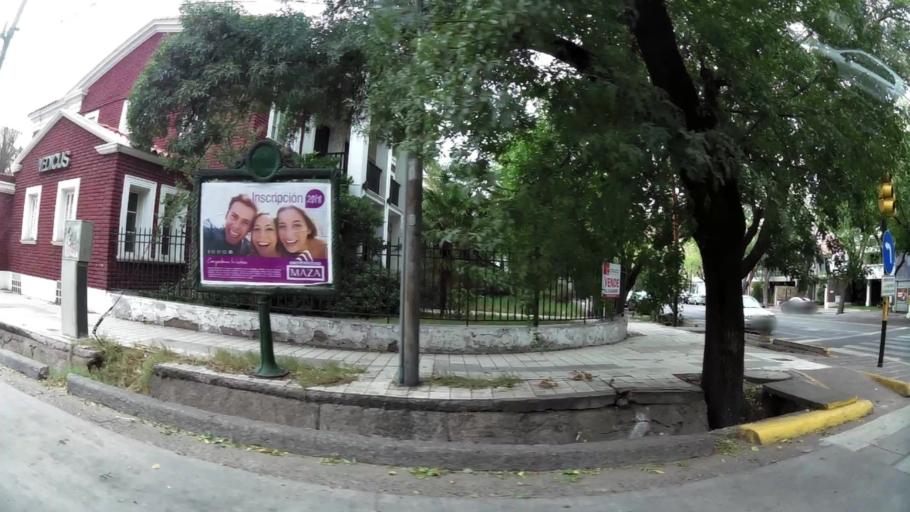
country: AR
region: Mendoza
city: Mendoza
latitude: -32.8869
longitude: -68.8590
